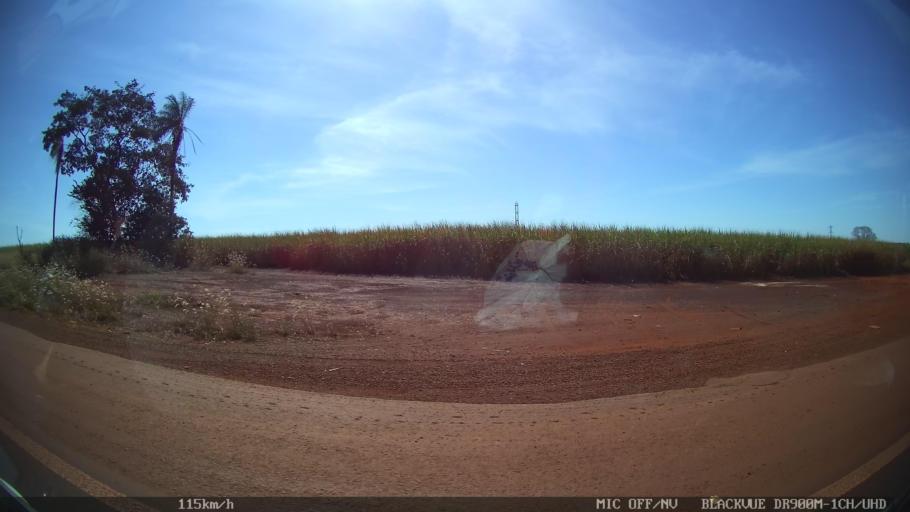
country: BR
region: Sao Paulo
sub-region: Guaira
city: Guaira
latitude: -20.4451
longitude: -48.3898
